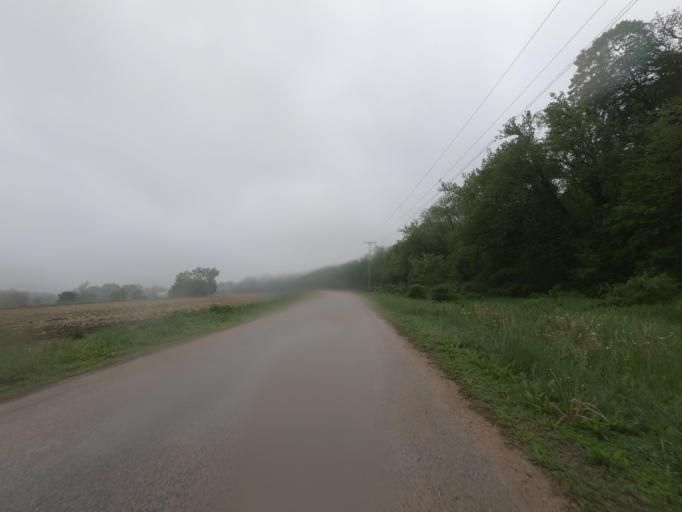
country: US
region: Wisconsin
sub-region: Grant County
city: Hazel Green
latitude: 42.5080
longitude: -90.4799
